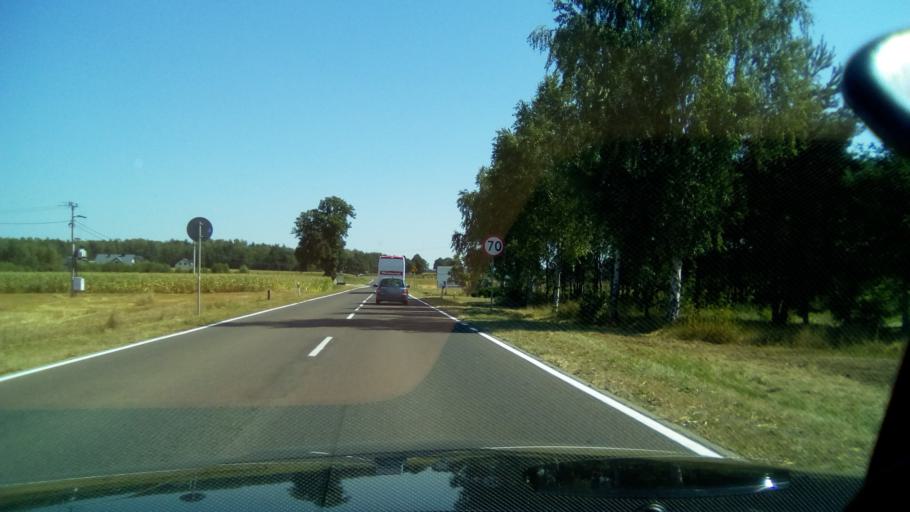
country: PL
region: Masovian Voivodeship
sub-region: Powiat plocki
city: Starozreby
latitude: 52.6393
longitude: 20.0207
